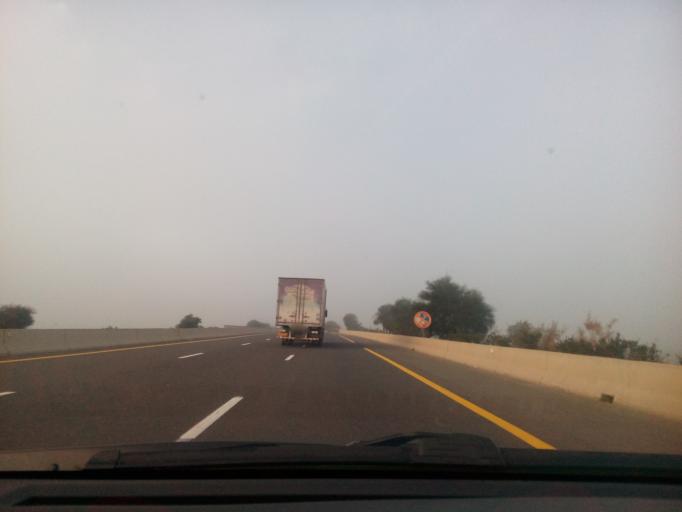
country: DZ
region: Relizane
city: Relizane
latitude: 35.7978
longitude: 0.5057
